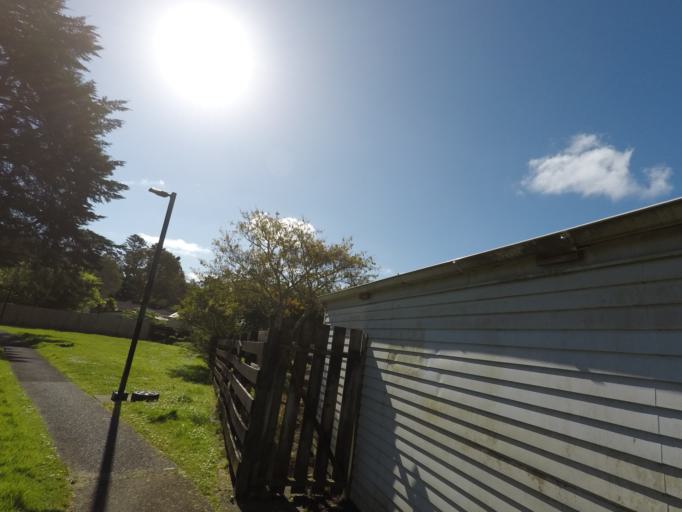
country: NZ
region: Auckland
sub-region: Auckland
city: Rosebank
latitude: -36.8616
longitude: 174.5964
